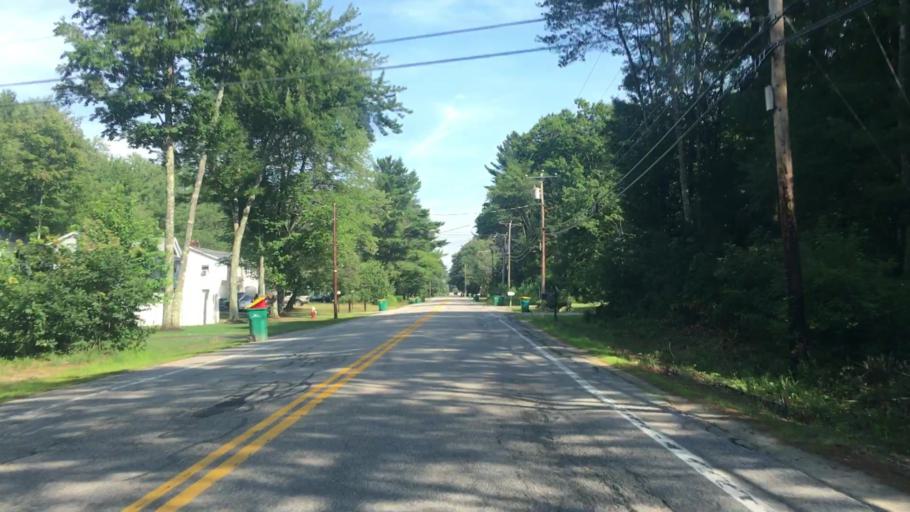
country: US
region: New Hampshire
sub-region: Strafford County
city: Rochester
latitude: 43.2802
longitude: -70.9691
